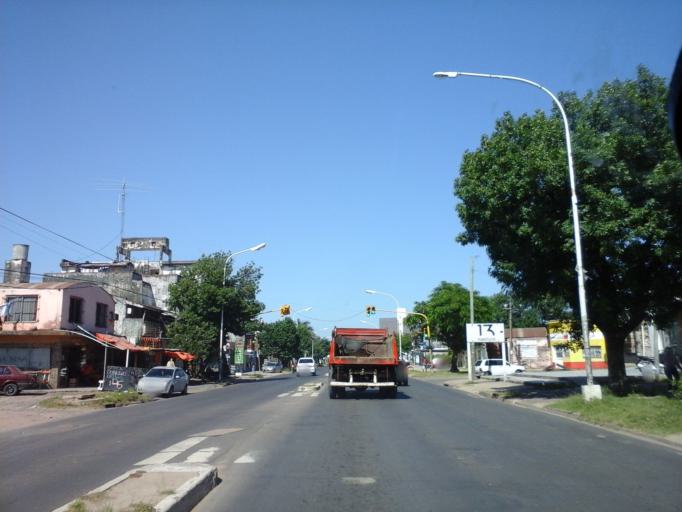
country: AR
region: Corrientes
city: Corrientes
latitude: -27.4685
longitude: -58.7973
